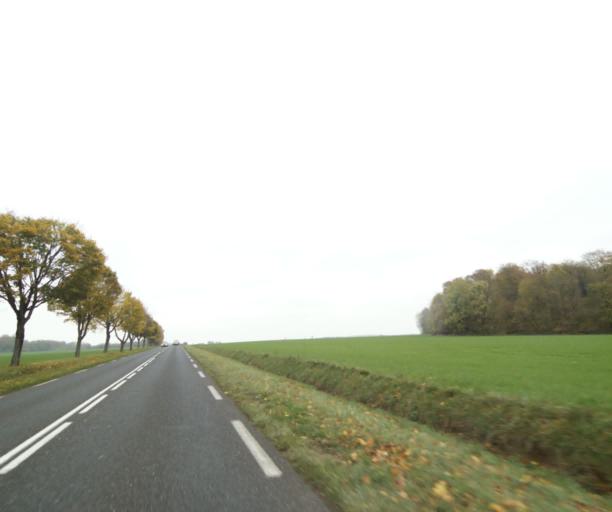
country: FR
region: Lorraine
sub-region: Departement de Meurthe-et-Moselle
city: Briey
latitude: 49.2753
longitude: 5.9590
